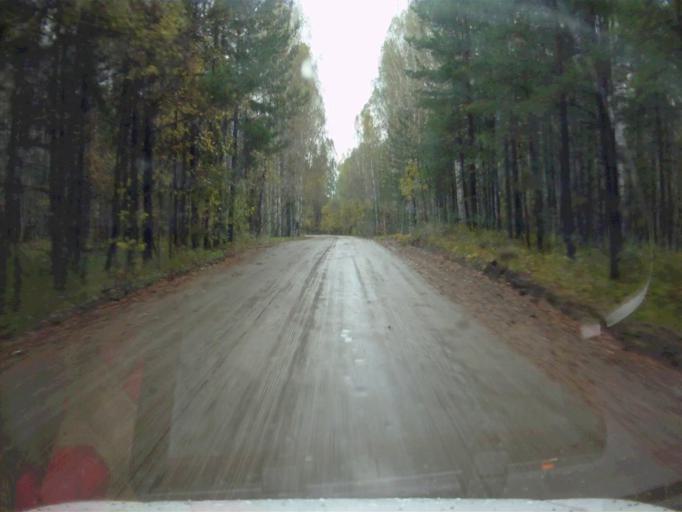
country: RU
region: Chelyabinsk
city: Kyshtym
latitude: 55.8399
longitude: 60.4867
